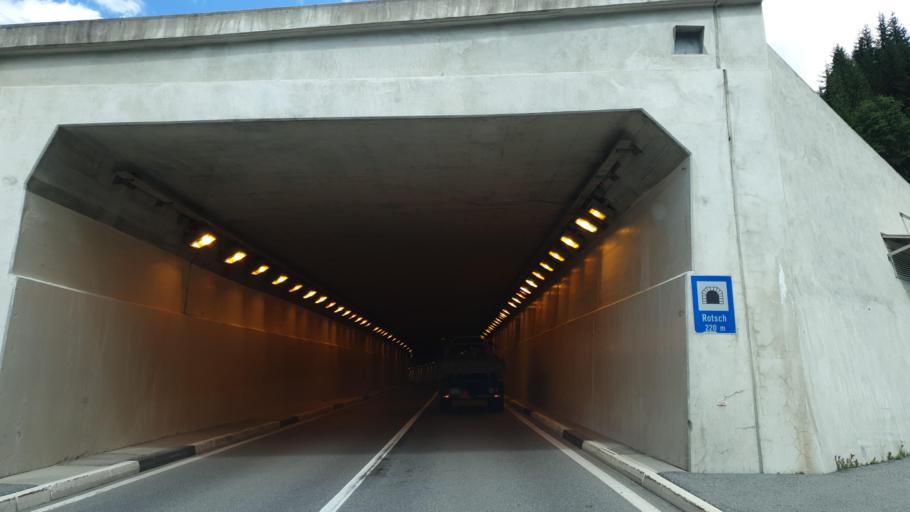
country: CH
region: Grisons
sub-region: Plessur District
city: Arosa
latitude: 46.7222
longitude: 9.7678
